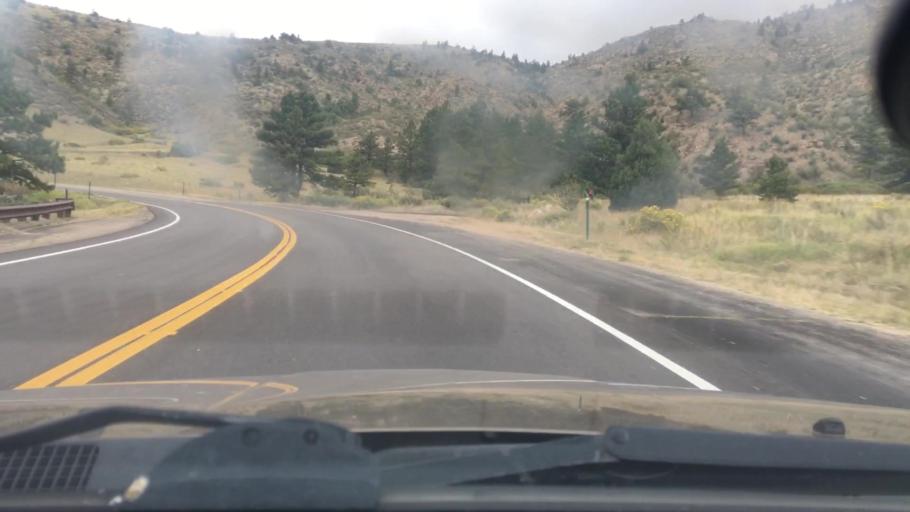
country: US
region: Colorado
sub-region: Larimer County
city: Laporte
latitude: 40.6979
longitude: -105.4416
